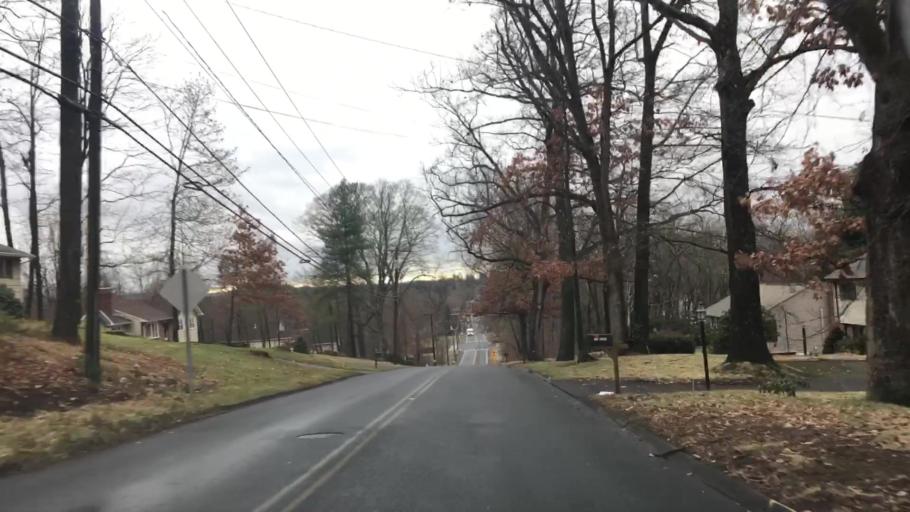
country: US
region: Connecticut
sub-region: Hartford County
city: Manchester
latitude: 41.8341
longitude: -72.5146
